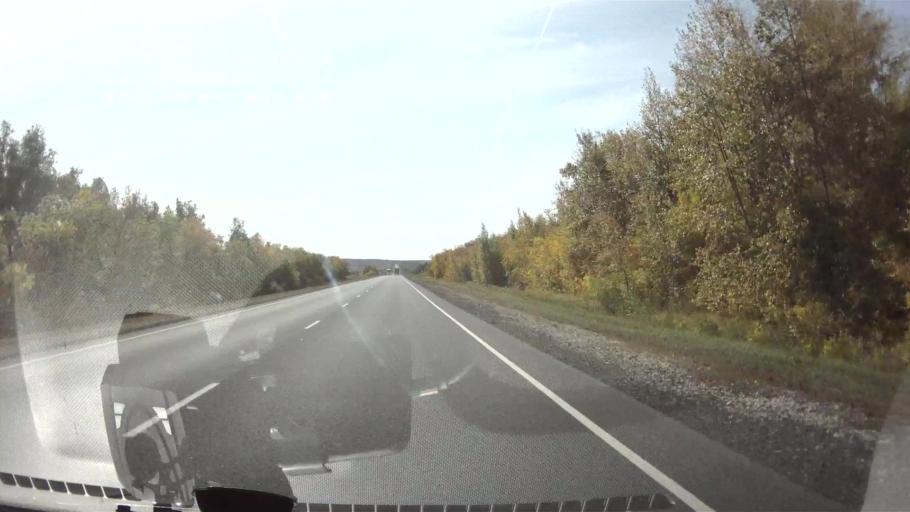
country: RU
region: Saratov
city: Khvalynsk
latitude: 52.5907
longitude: 48.1302
